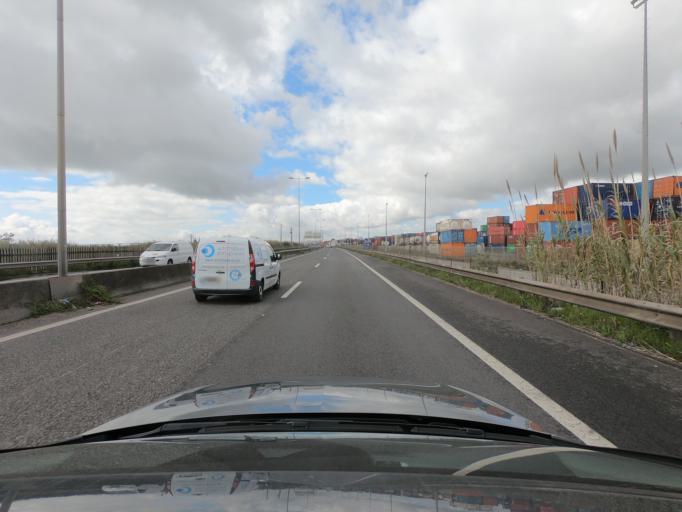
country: PT
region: Lisbon
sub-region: Loures
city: Sao Joao da Talha
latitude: 38.8250
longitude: -9.0835
